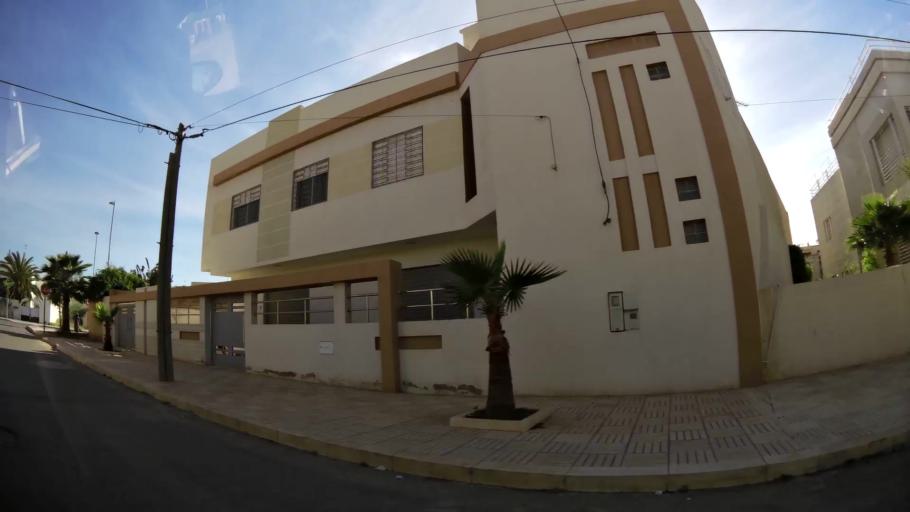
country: MA
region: Oriental
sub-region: Oujda-Angad
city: Oujda
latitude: 34.6641
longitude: -1.9048
